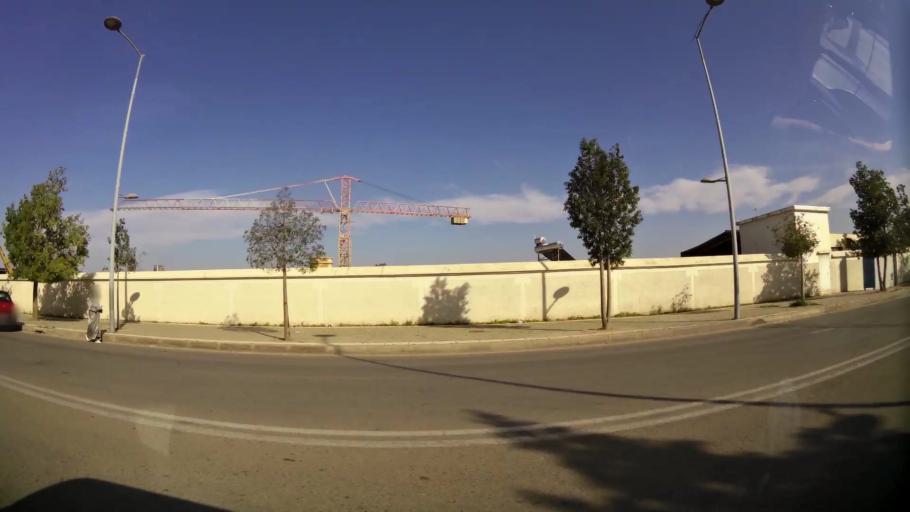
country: MA
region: Oriental
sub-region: Oujda-Angad
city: Oujda
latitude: 34.7090
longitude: -1.8908
